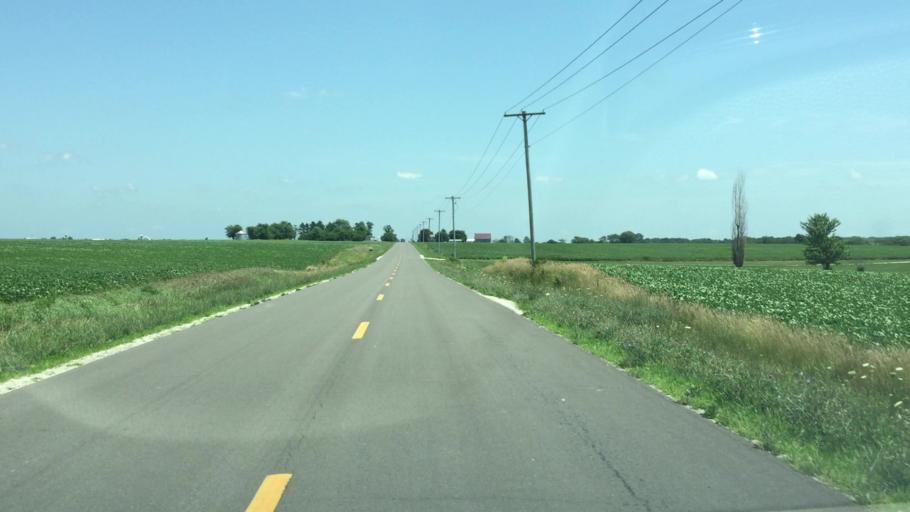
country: US
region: Illinois
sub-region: Hancock County
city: Carthage
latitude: 40.3280
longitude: -91.1799
